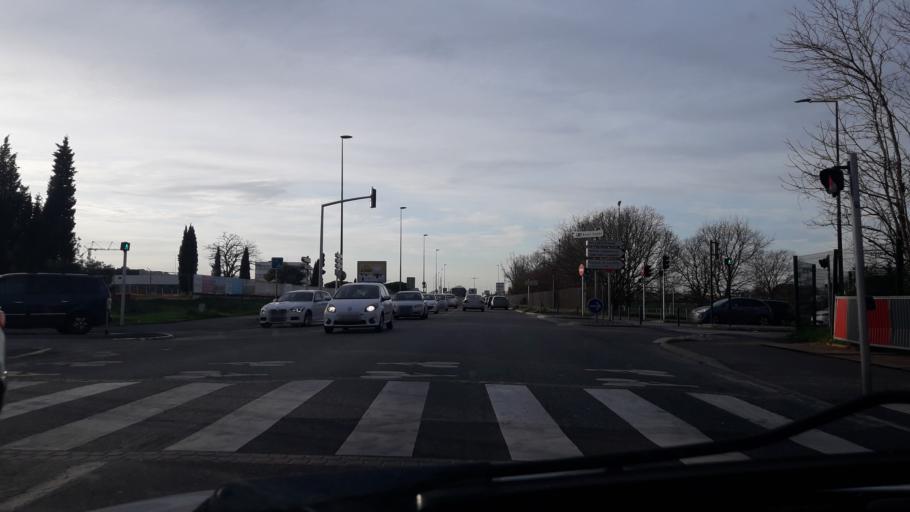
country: FR
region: Midi-Pyrenees
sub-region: Departement de la Haute-Garonne
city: Portet-sur-Garonne
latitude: 43.5598
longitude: 1.3953
